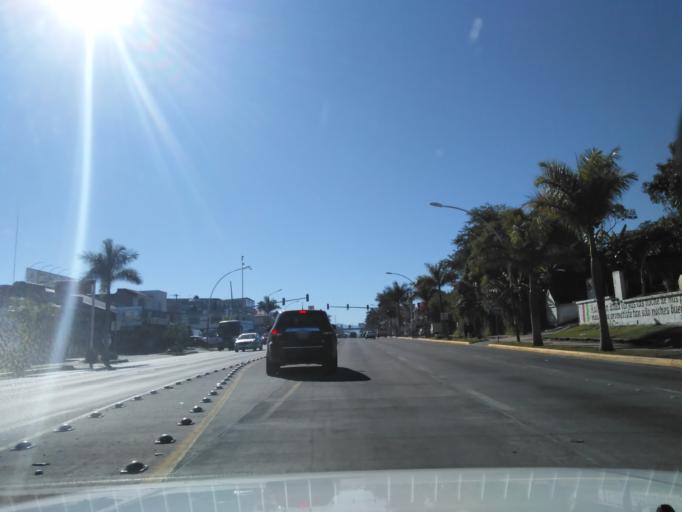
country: MX
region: Nayarit
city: Xalisco
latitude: 21.4766
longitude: -104.8908
